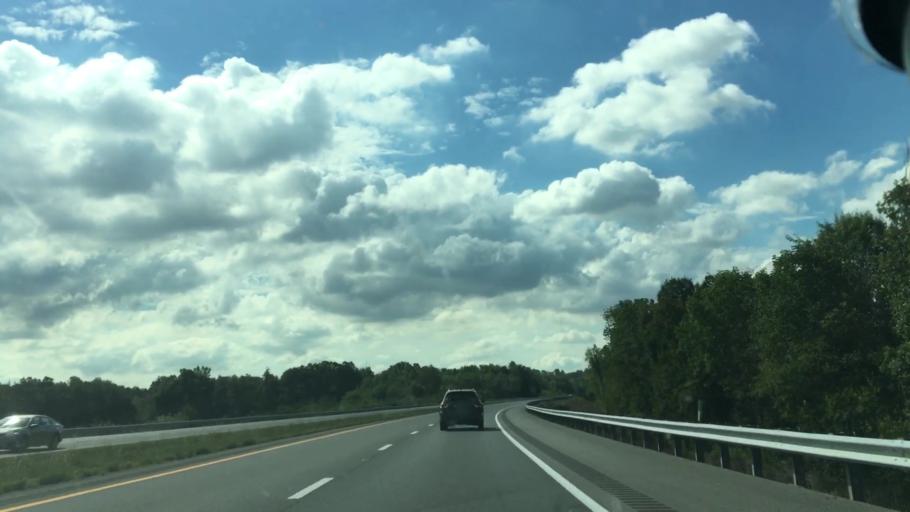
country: US
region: Kentucky
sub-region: Webster County
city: Sebree
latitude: 37.5697
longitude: -87.4783
